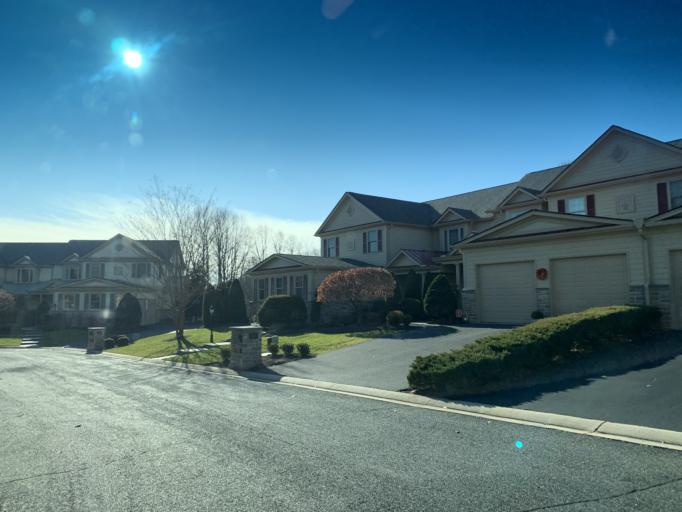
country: US
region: Maryland
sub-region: Harford County
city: Bel Air South
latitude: 39.5151
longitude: -76.3025
